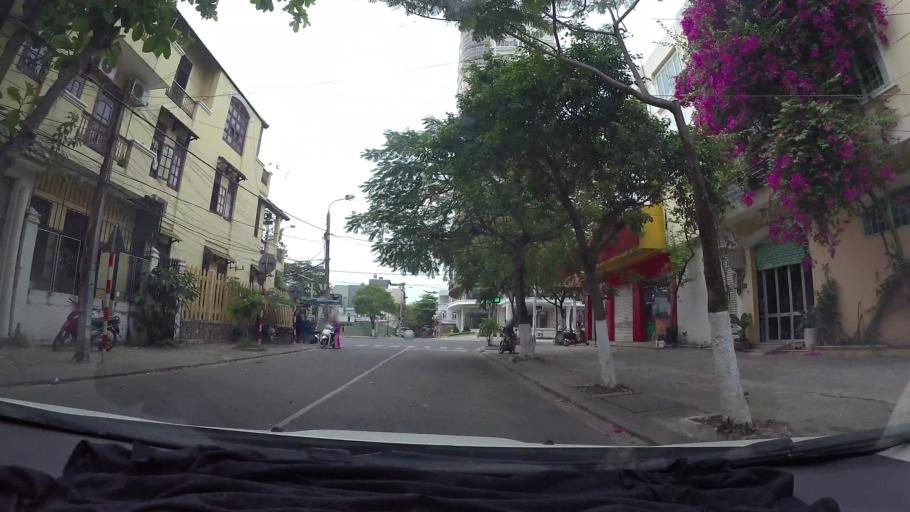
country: VN
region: Da Nang
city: Da Nang
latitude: 16.0864
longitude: 108.2184
